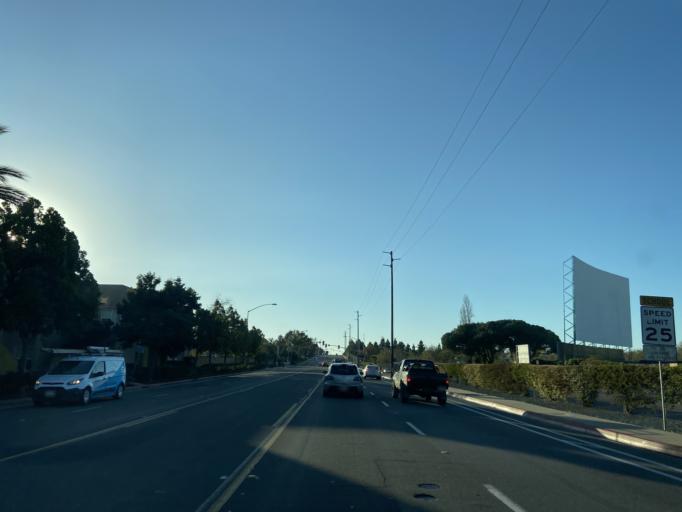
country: US
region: California
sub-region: San Diego County
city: Imperial Beach
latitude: 32.5765
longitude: -117.0866
